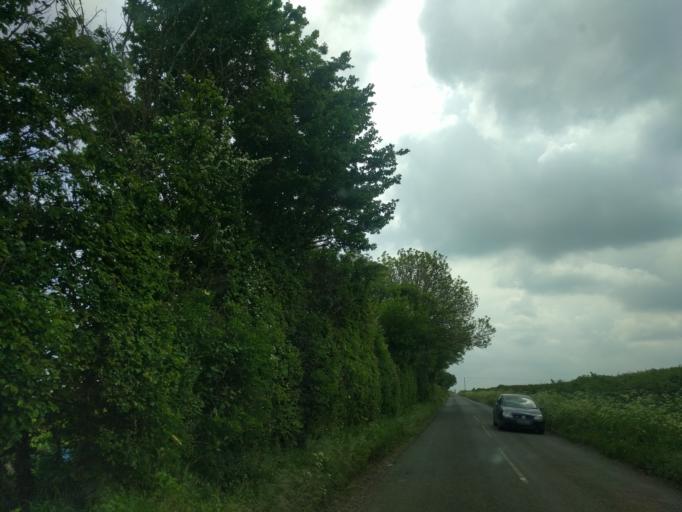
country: GB
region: England
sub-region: Somerset
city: Langport
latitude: 51.0562
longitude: -2.8123
